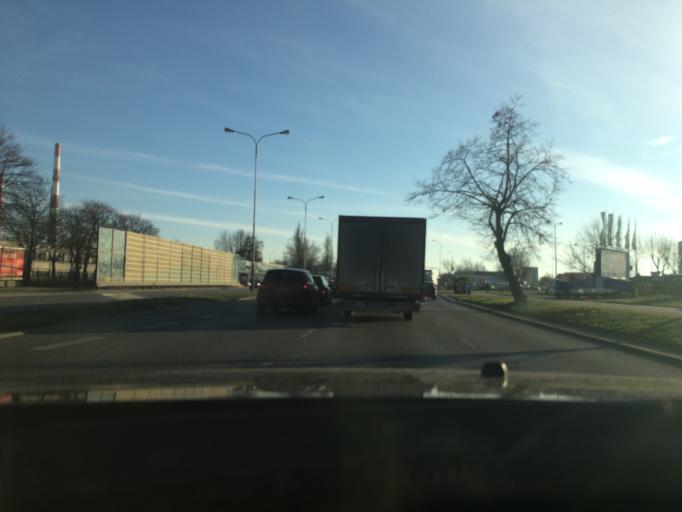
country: PL
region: Lodz Voivodeship
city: Lodz
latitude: 51.7465
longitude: 19.4396
